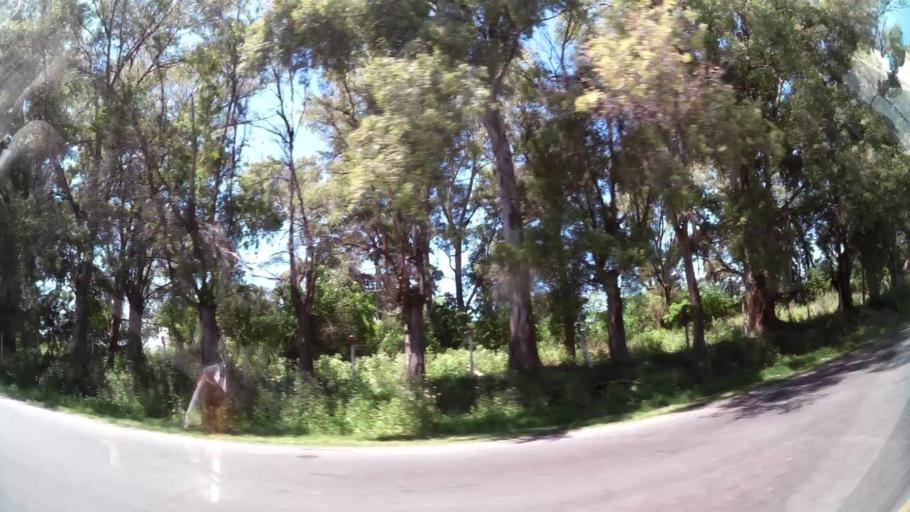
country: AR
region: Buenos Aires
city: Hurlingham
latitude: -34.5097
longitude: -58.6587
